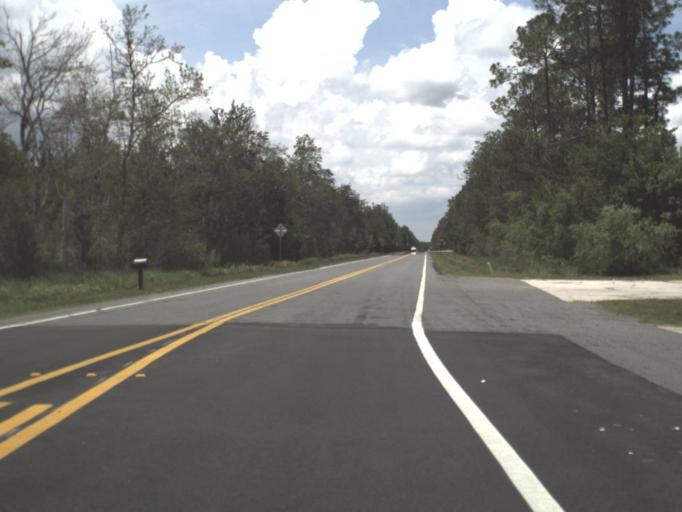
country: US
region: Georgia
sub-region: Camden County
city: Kingsland
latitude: 30.7166
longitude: -81.6756
